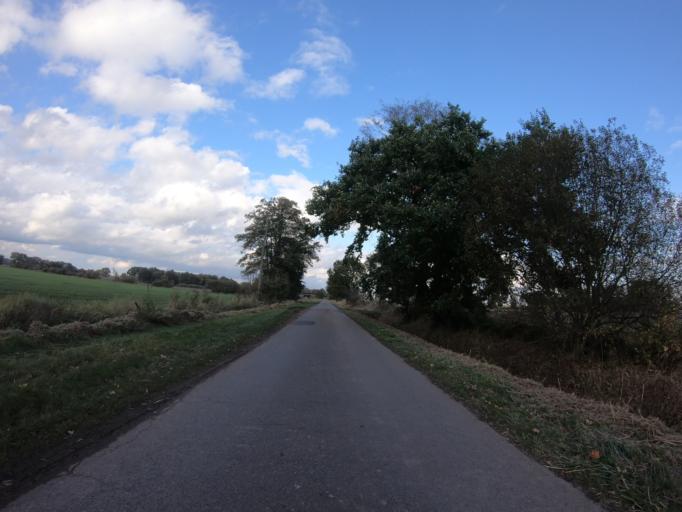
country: DE
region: Lower Saxony
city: Wagenhoff
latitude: 52.5264
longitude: 10.5414
